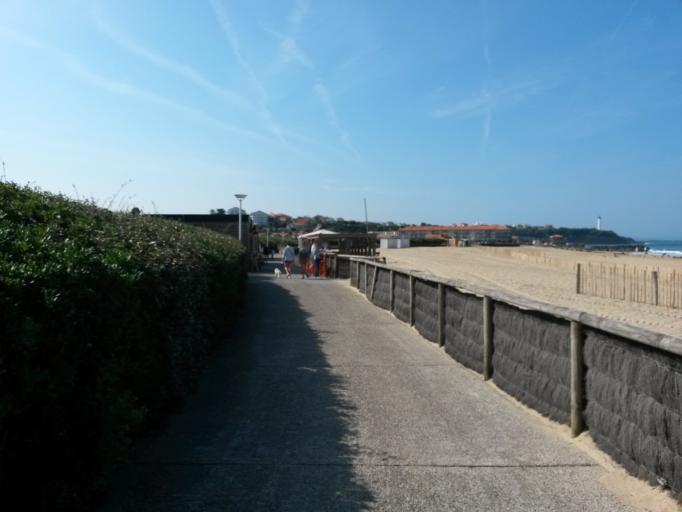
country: FR
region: Aquitaine
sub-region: Departement des Pyrenees-Atlantiques
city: Biarritz
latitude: 43.5041
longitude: -1.5384
